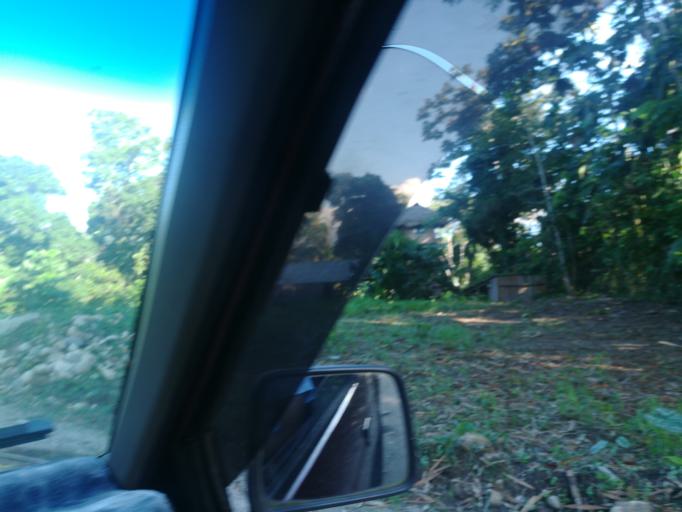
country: EC
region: Napo
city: Tena
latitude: -0.9922
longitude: -77.8257
